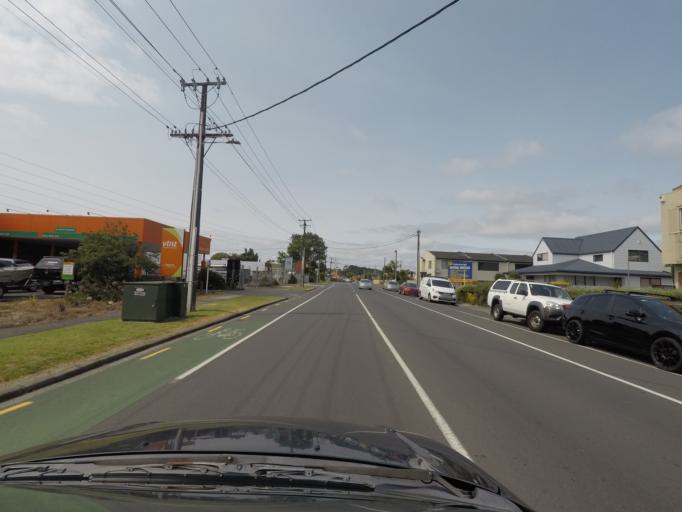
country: NZ
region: Auckland
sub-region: Auckland
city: Waitakere
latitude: -36.9143
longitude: 174.6905
